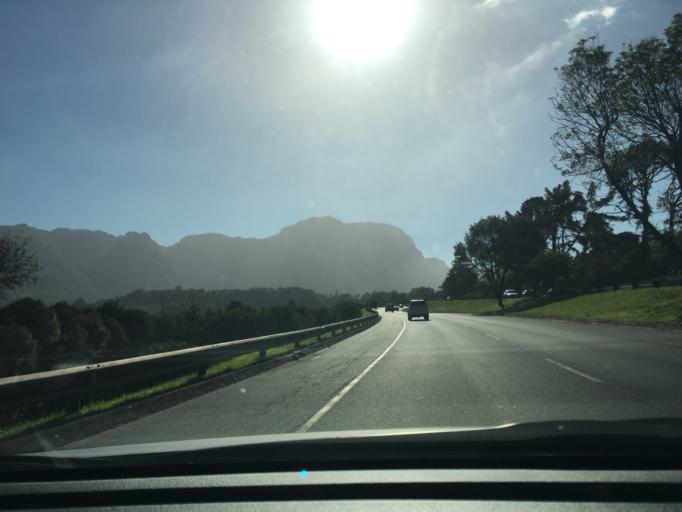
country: ZA
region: Western Cape
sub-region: City of Cape Town
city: Newlands
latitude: -34.0078
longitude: 18.4520
